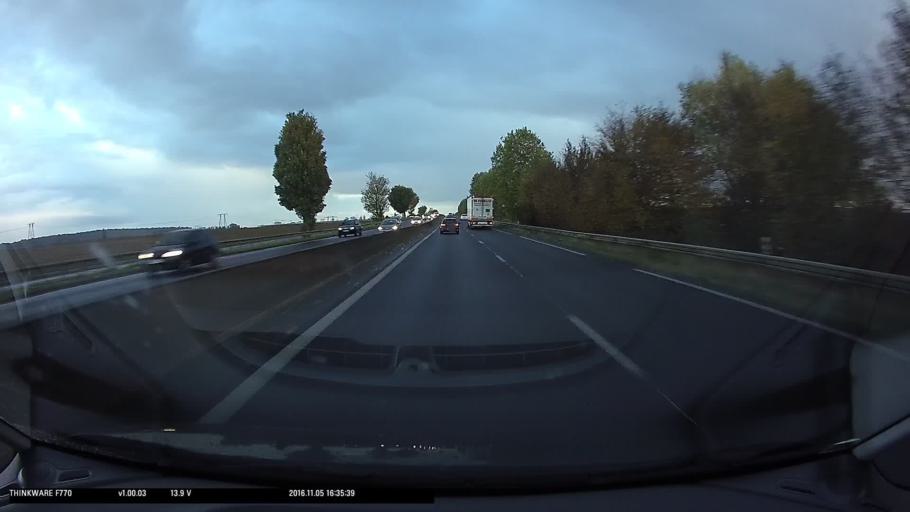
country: FR
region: Ile-de-France
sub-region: Departement du Val-d'Oise
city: Ableiges
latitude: 49.0630
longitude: 1.9860
